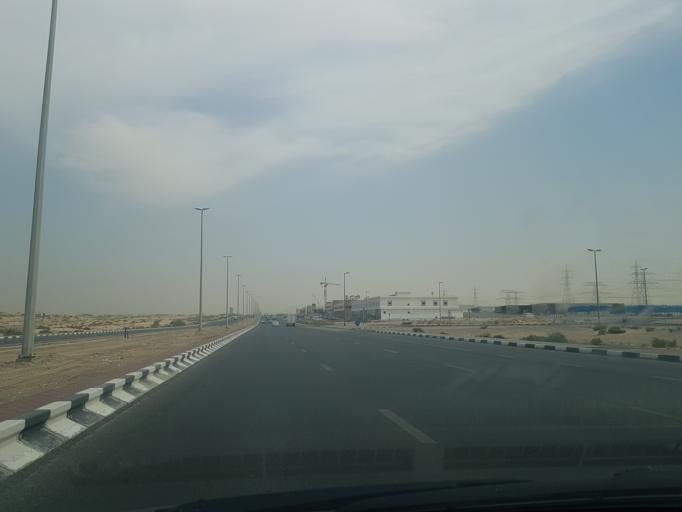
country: AE
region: Ash Shariqah
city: Sharjah
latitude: 25.2597
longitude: 55.5100
